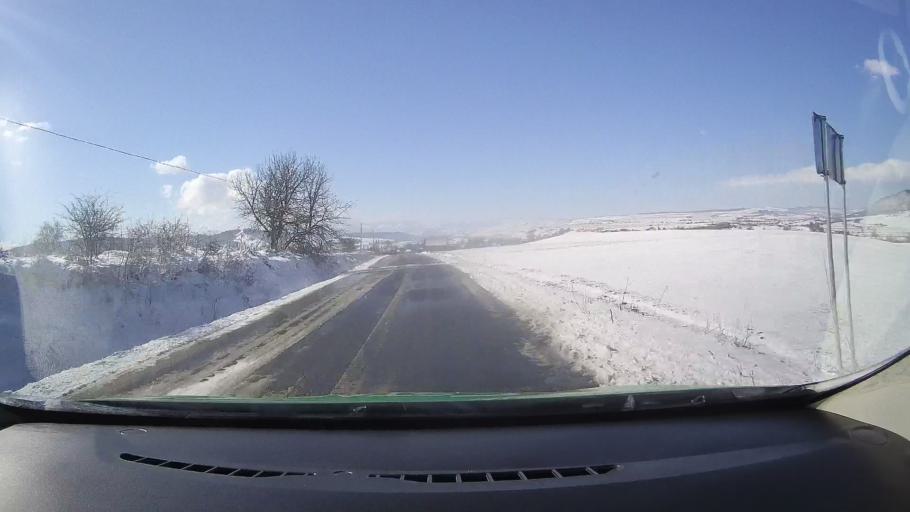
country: RO
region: Sibiu
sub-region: Comuna Rosia
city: Rosia
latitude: 45.8024
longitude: 24.3642
